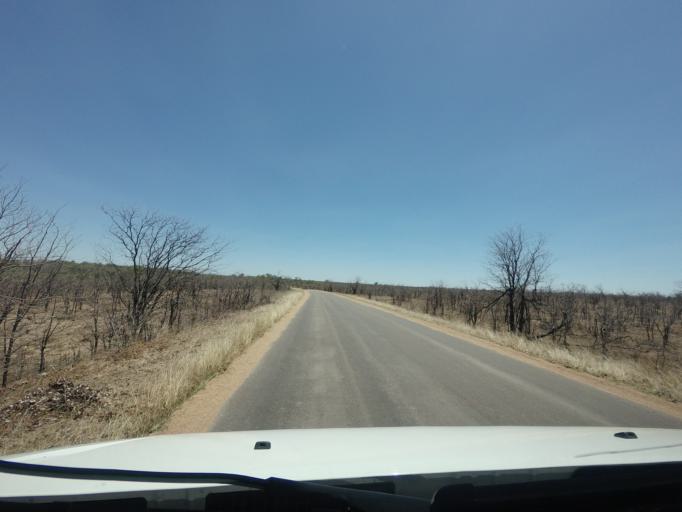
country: ZA
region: Limpopo
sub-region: Mopani District Municipality
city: Phalaborwa
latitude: -23.5578
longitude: 31.4492
